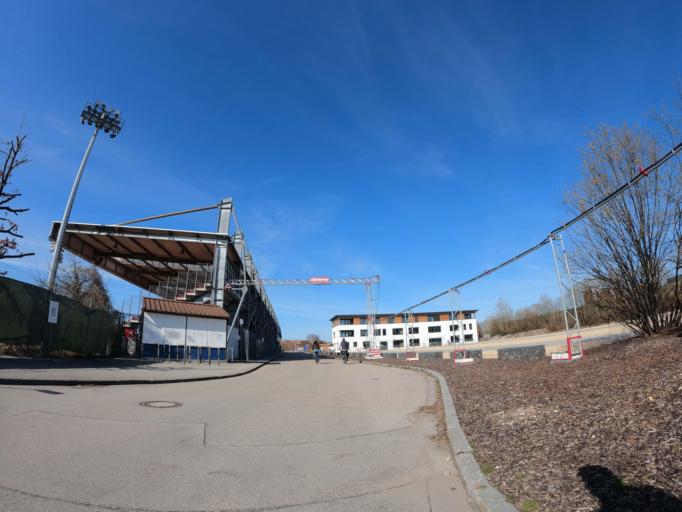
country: DE
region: Bavaria
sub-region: Upper Bavaria
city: Unterhaching
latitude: 48.0729
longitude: 11.6166
